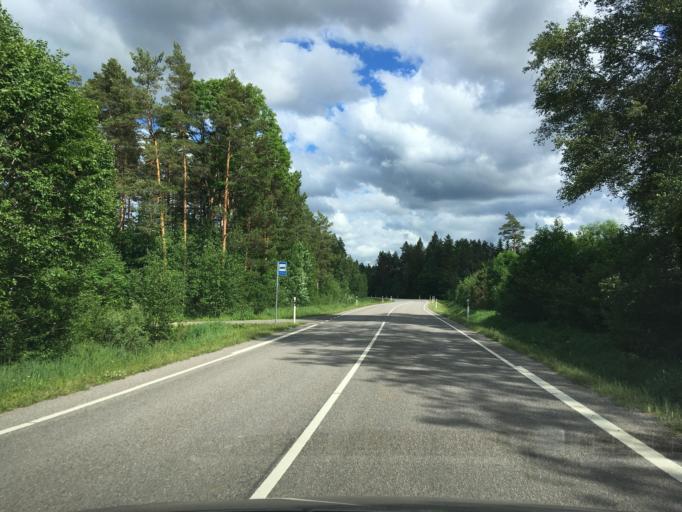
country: EE
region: Paernumaa
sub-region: Tootsi vald
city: Tootsi
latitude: 58.6624
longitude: 24.6709
